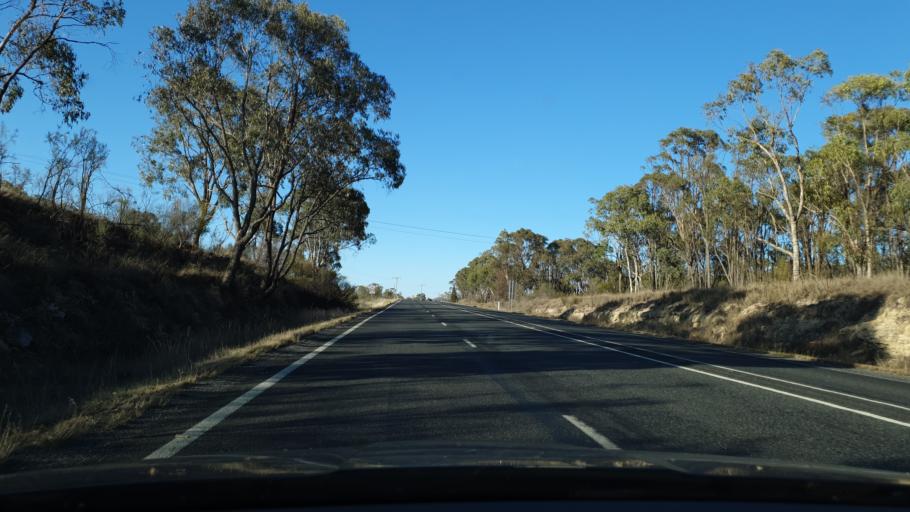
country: AU
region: Queensland
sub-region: Southern Downs
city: Stanthorpe
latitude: -28.6951
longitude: 151.9068
